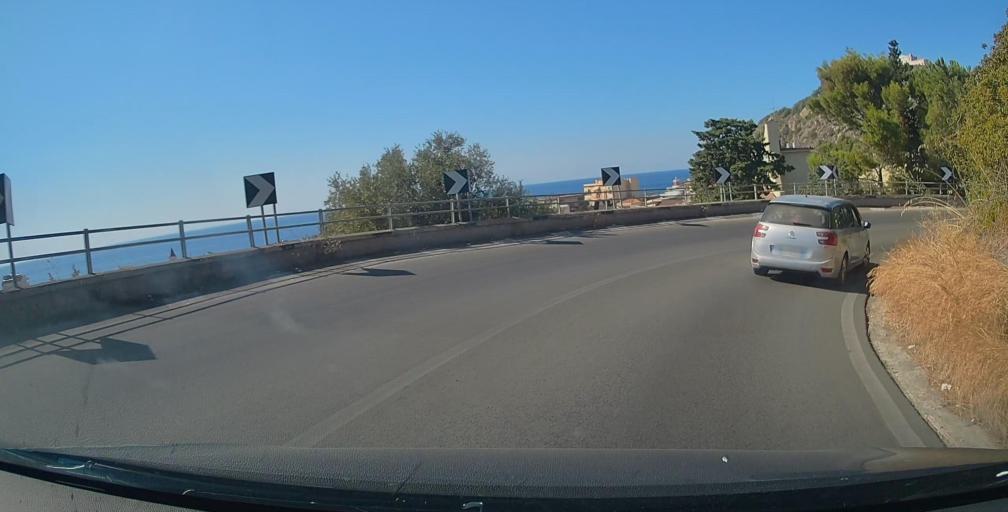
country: IT
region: Sicily
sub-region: Messina
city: Capo d'Orlando
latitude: 38.1602
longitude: 14.7473
